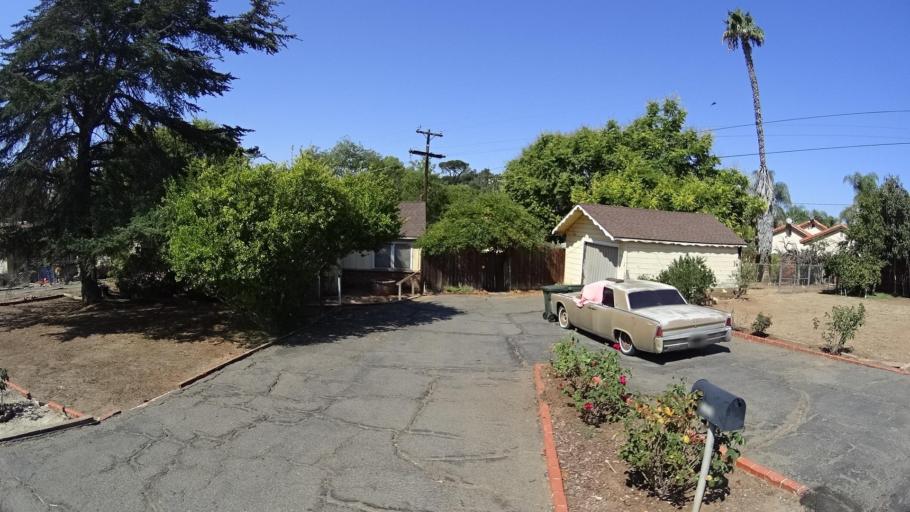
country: US
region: California
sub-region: San Diego County
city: Vista
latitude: 33.1795
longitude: -117.2098
